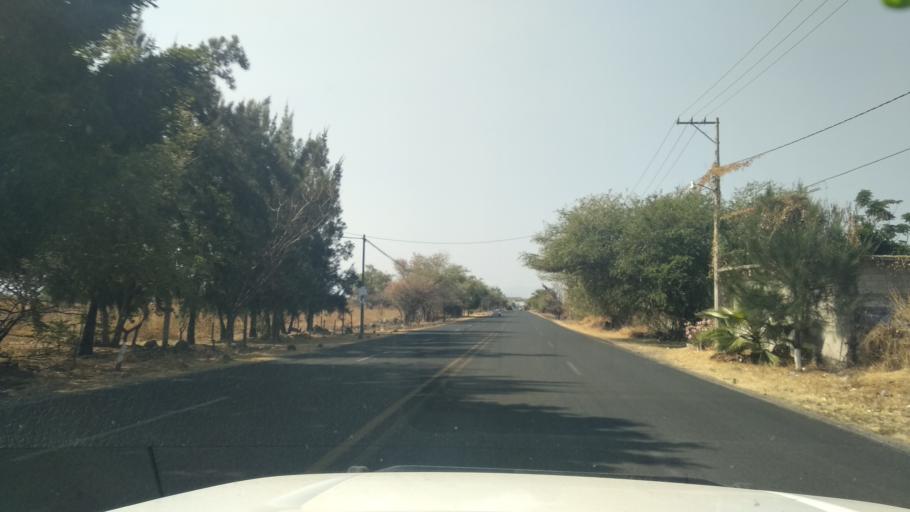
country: MX
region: Morelos
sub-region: Temoac
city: Huazulco
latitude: 18.7420
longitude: -98.7850
